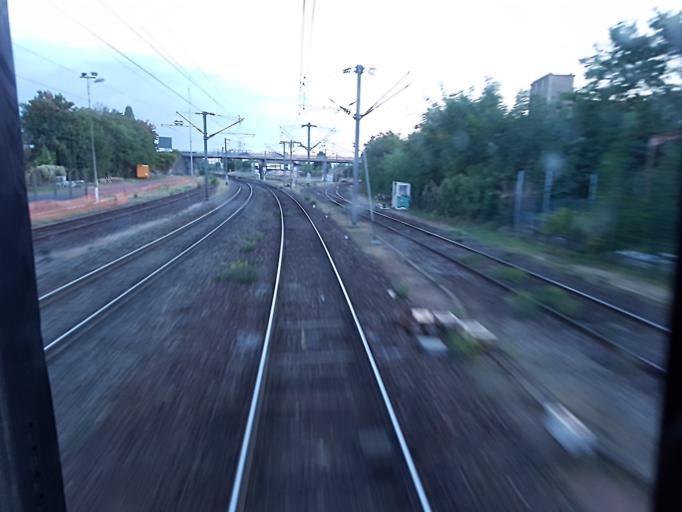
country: FR
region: Auvergne
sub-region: Departement du Puy-de-Dome
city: Riom
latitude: 45.8877
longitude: 3.1204
